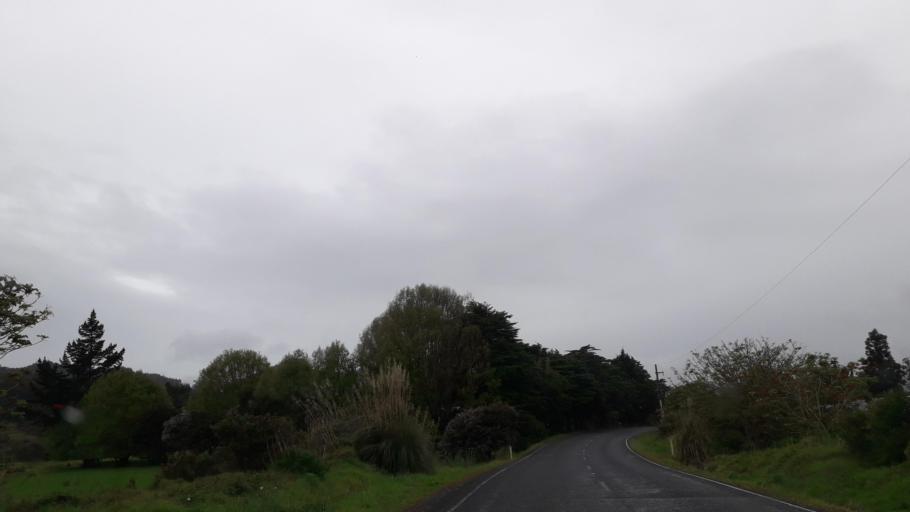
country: NZ
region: Northland
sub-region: Far North District
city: Kaitaia
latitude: -35.3709
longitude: 173.5008
